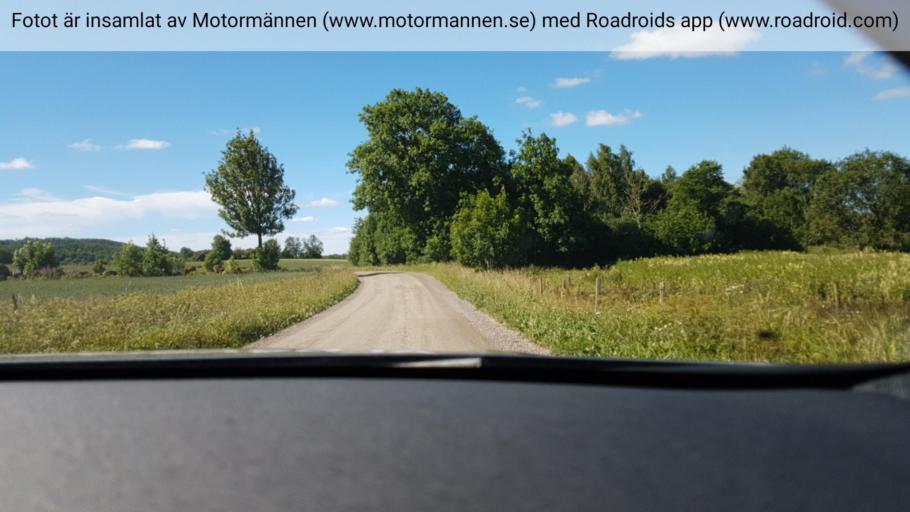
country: SE
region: Vaestra Goetaland
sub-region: Falkopings Kommun
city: Akarp
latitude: 58.2017
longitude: 13.7347
